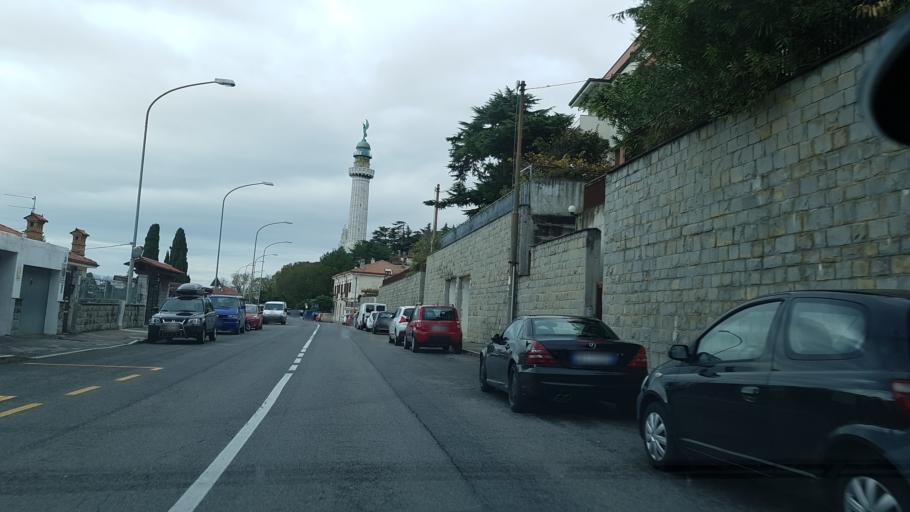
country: IT
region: Friuli Venezia Giulia
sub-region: Provincia di Trieste
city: Villa Opicina
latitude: 45.6739
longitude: 13.7591
